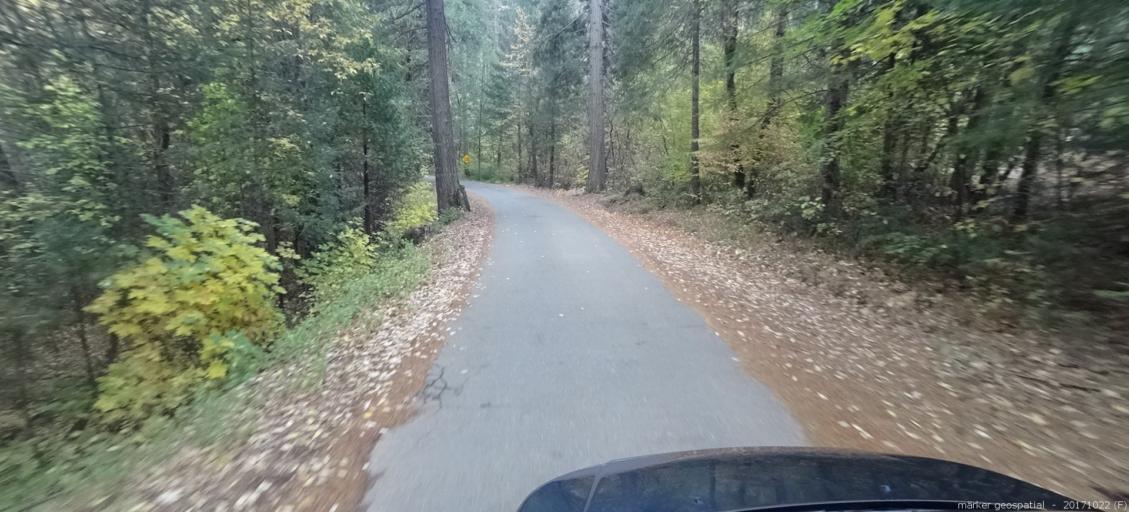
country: US
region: California
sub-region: Siskiyou County
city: Dunsmuir
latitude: 41.1697
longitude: -122.2704
